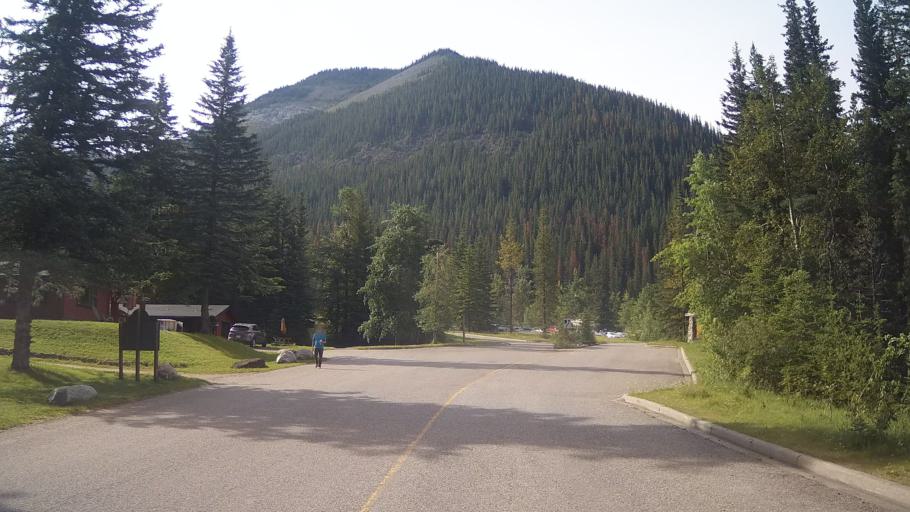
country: CA
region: Alberta
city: Hinton
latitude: 53.1318
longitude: -117.7716
